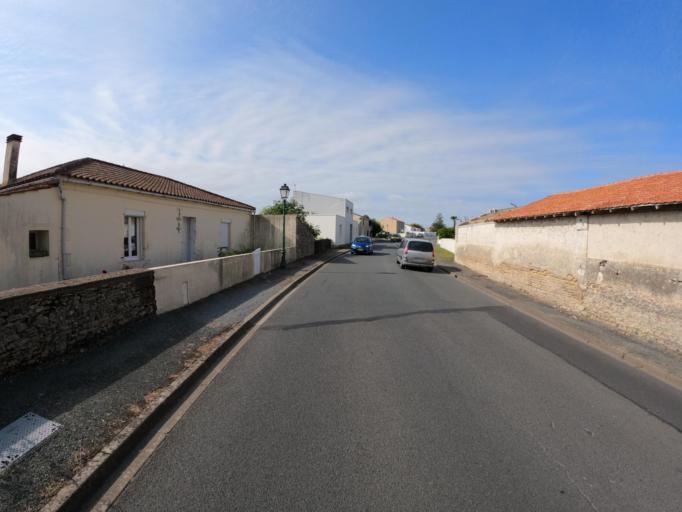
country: FR
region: Pays de la Loire
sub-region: Departement de la Vendee
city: Triaize
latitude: 46.3586
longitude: -1.2426
